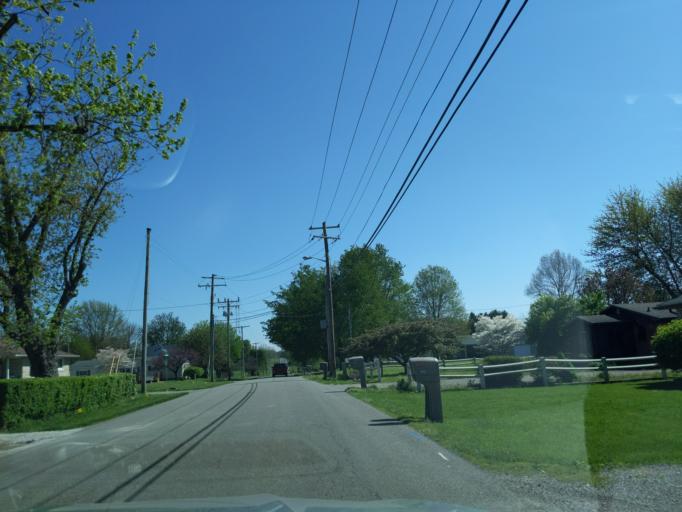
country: US
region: Indiana
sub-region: Decatur County
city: Greensburg
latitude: 39.3288
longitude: -85.4889
